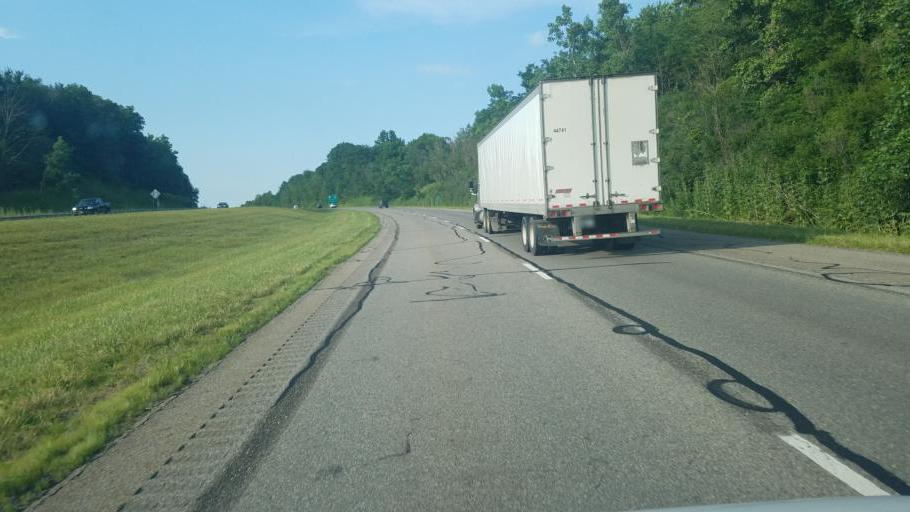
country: US
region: Ohio
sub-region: Summit County
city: Boston Heights
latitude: 41.2823
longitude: -81.5275
